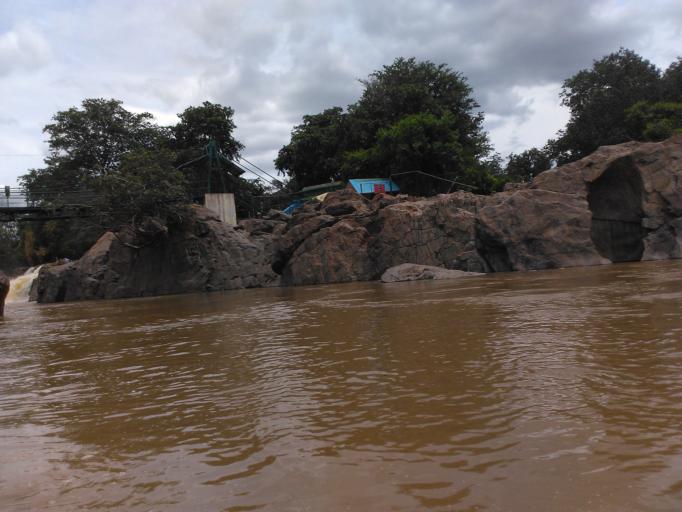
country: IN
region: Tamil Nadu
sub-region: Dharmapuri
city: Pennagaram
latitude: 12.1151
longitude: 77.7782
